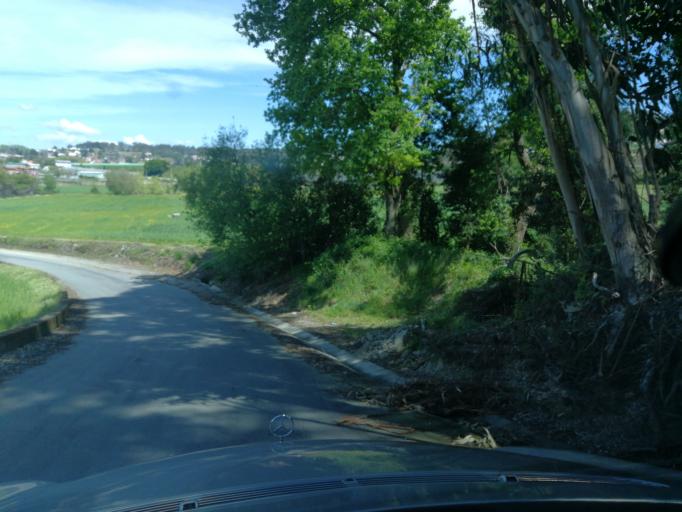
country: PT
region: Braga
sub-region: Vila Nova de Famalicao
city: Vila Nova de Famalicao
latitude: 41.4284
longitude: -8.5266
